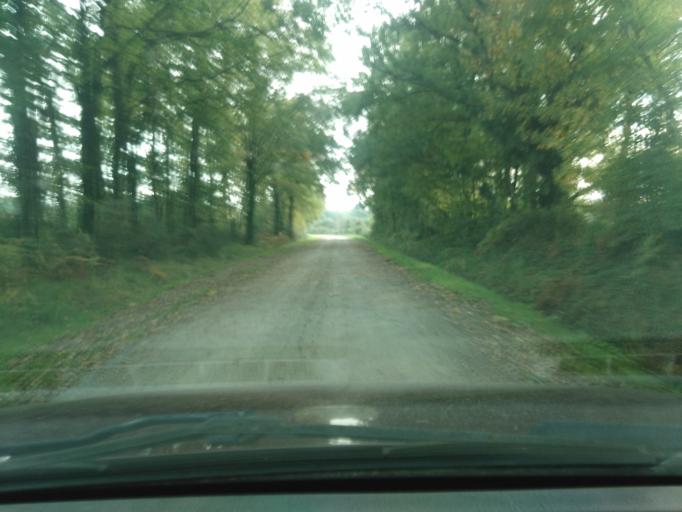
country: FR
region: Pays de la Loire
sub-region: Departement de la Vendee
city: Mouilleron-le-Captif
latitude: 46.7165
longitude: -1.4169
